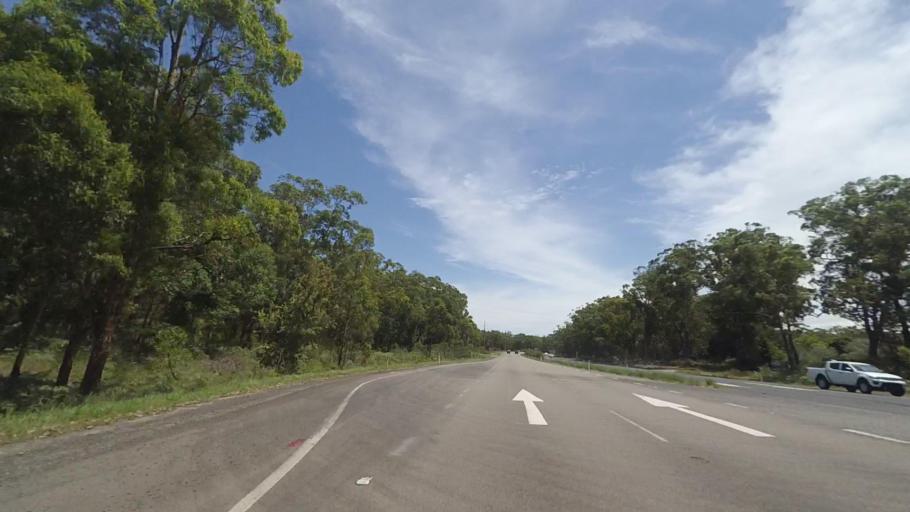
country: AU
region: New South Wales
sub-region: Port Stephens Shire
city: Anna Bay
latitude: -32.7757
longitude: 152.0051
